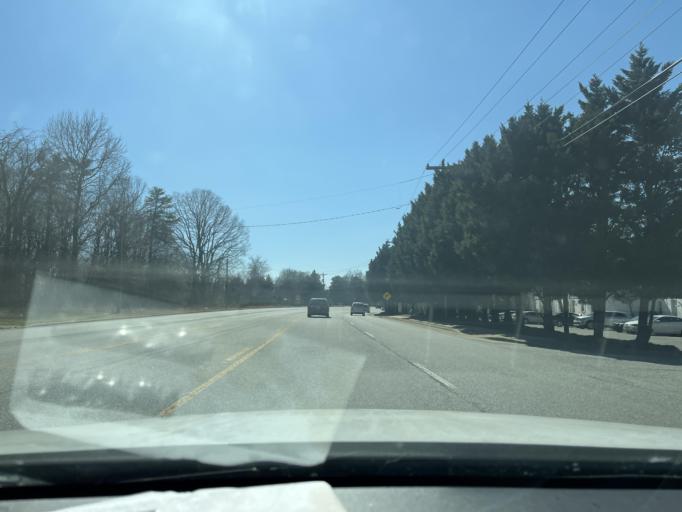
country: US
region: North Carolina
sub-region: Guilford County
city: Jamestown
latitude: 36.0569
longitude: -79.9120
